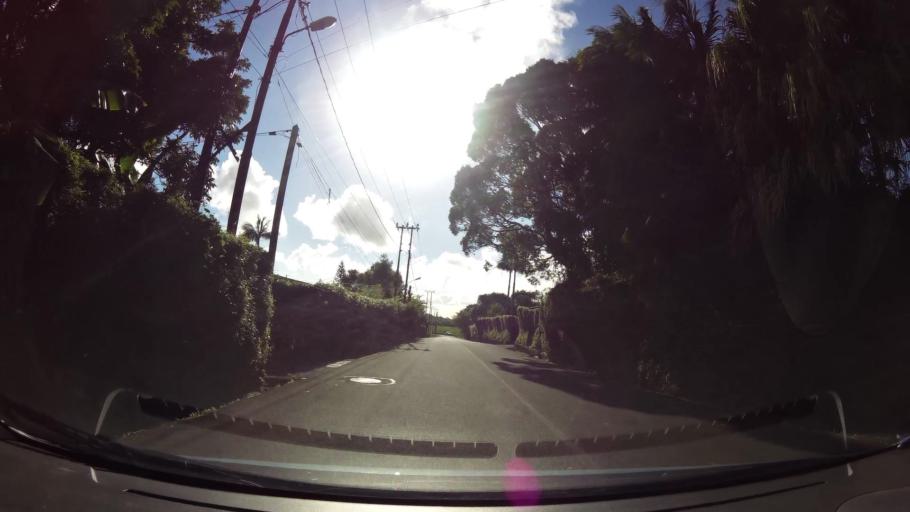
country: MU
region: Plaines Wilhems
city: Curepipe
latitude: -20.3149
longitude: 57.5374
